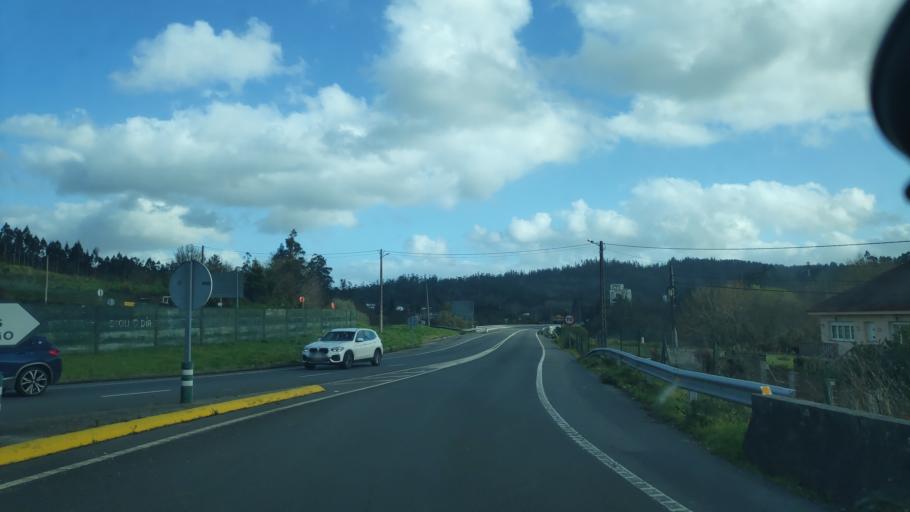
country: ES
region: Galicia
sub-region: Provincia da Coruna
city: Negreira
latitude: 42.9027
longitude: -8.7076
